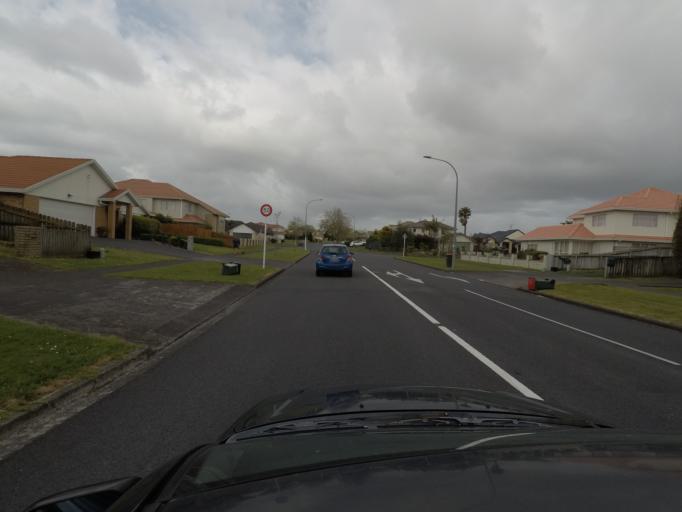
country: NZ
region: Auckland
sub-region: Auckland
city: Pakuranga
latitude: -36.9262
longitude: 174.9134
